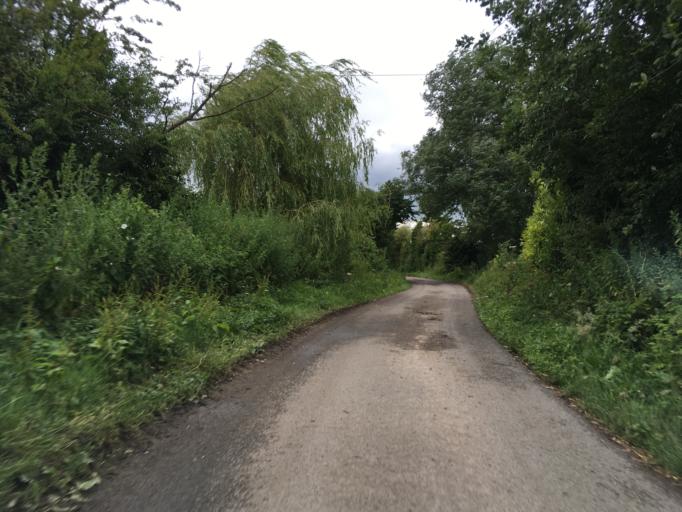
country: GB
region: England
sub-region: Gloucestershire
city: Cinderford
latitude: 51.7954
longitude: -2.4081
